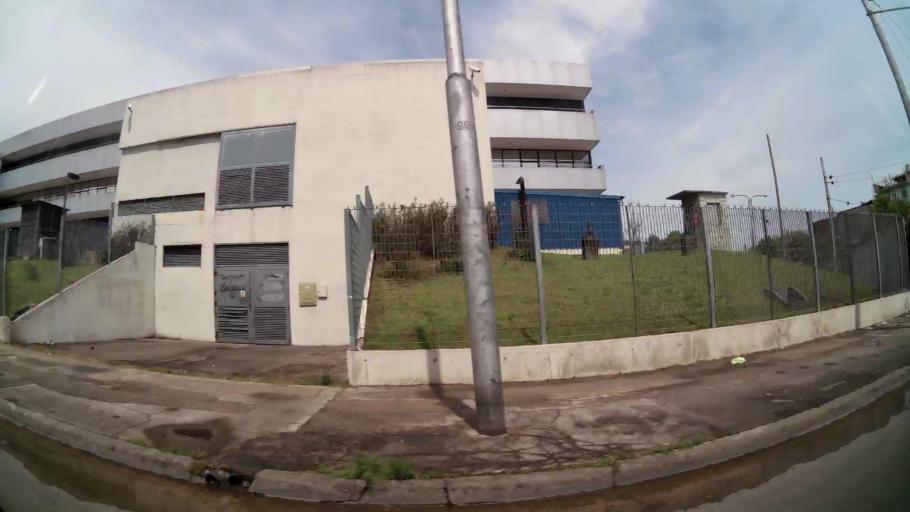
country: AR
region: Buenos Aires F.D.
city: Villa Lugano
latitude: -34.6538
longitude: -58.4566
